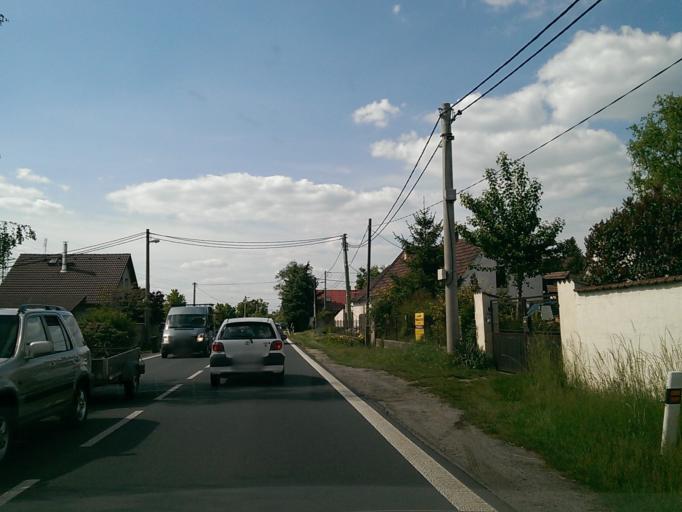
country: CZ
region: Central Bohemia
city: Libis
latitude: 50.3190
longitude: 14.5086
